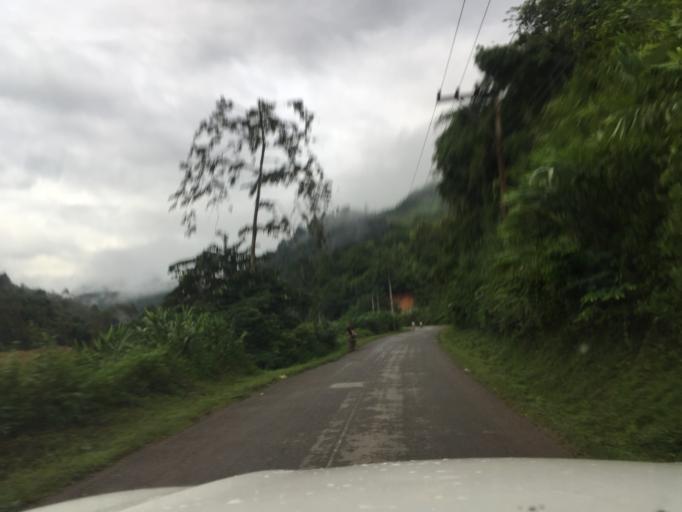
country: LA
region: Oudomxai
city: Muang La
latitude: 20.9134
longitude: 102.1913
